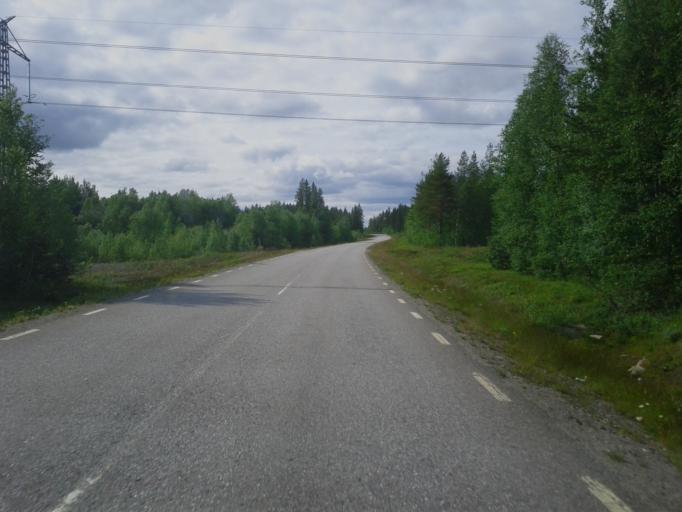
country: SE
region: Vaesterbotten
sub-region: Sorsele Kommun
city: Sorsele
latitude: 65.2814
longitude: 17.8871
